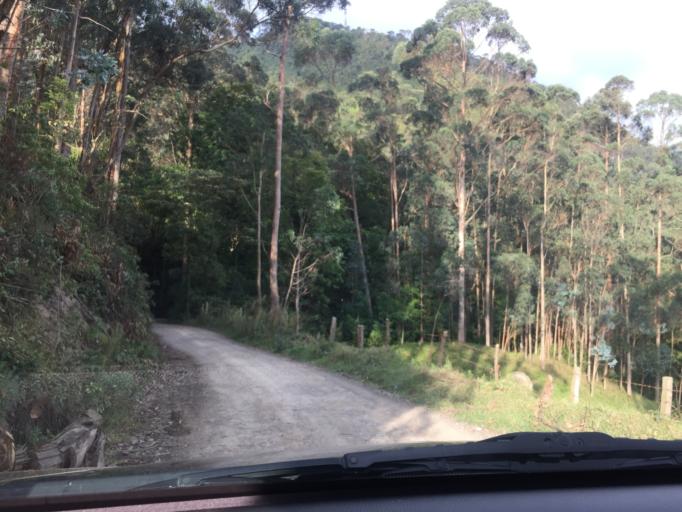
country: CO
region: Cundinamarca
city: Zipacon
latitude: 4.7437
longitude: -74.3932
